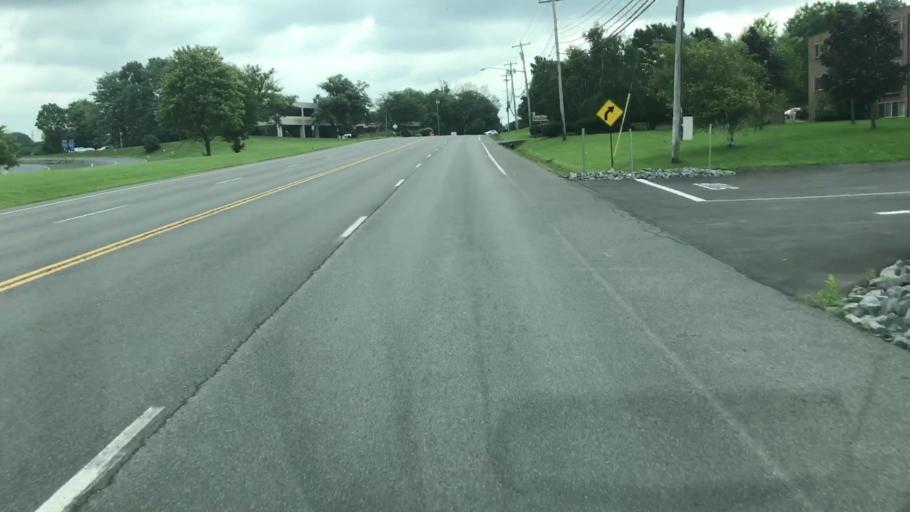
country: US
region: New York
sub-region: Onondaga County
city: Galeville
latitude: 43.1005
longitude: -76.1850
